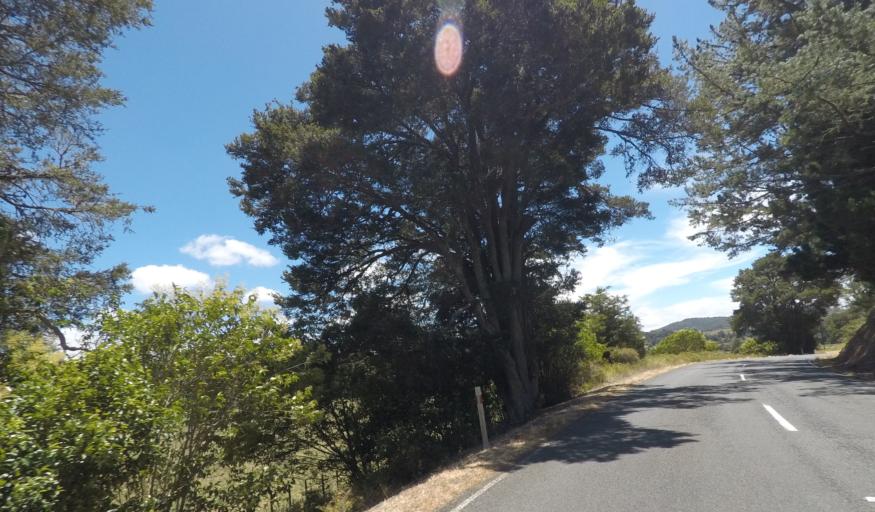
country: NZ
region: Northland
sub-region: Whangarei
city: Whangarei
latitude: -35.5385
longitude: 174.3100
